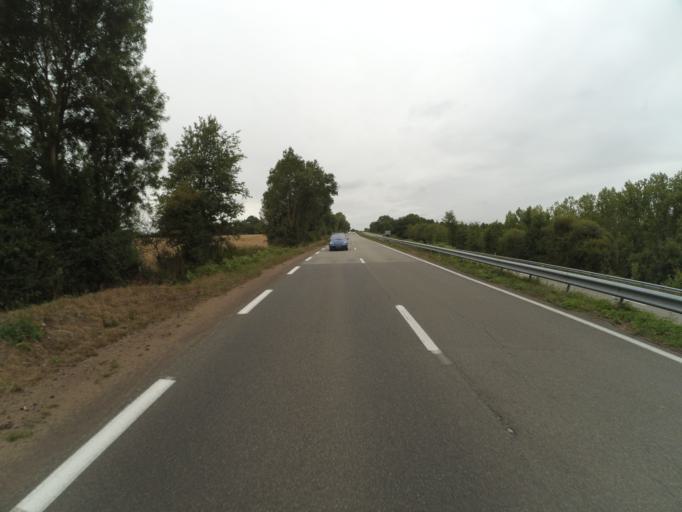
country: FR
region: Pays de la Loire
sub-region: Departement de la Vendee
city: Saligny
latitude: 46.8261
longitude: -1.4283
